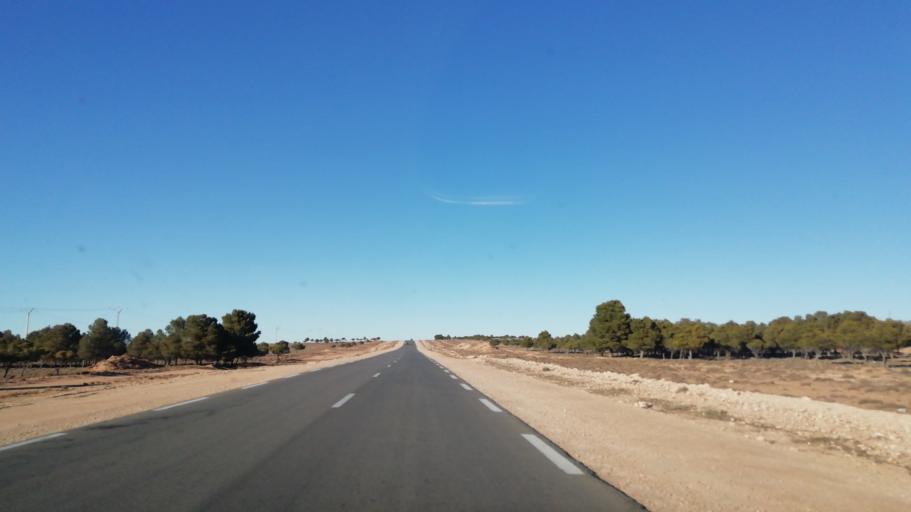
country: DZ
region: Tlemcen
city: Sebdou
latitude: 34.2533
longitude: -1.2575
